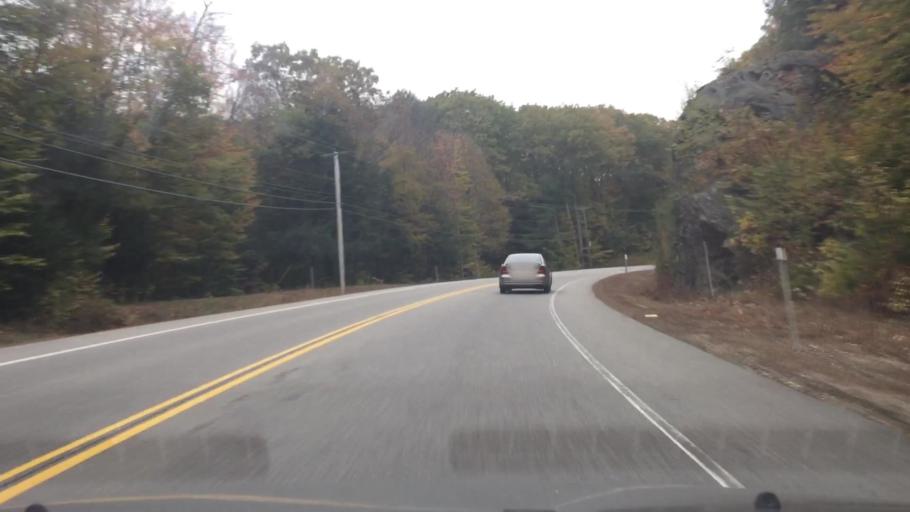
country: US
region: New Hampshire
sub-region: Cheshire County
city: Keene
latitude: 43.0229
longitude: -72.2682
